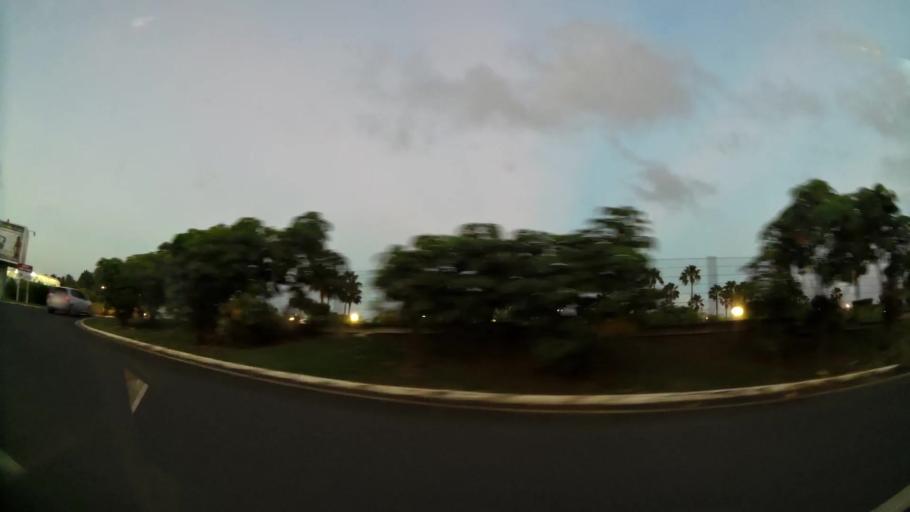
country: GP
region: Guadeloupe
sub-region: Guadeloupe
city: Les Abymes
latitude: 16.2639
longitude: -61.5147
